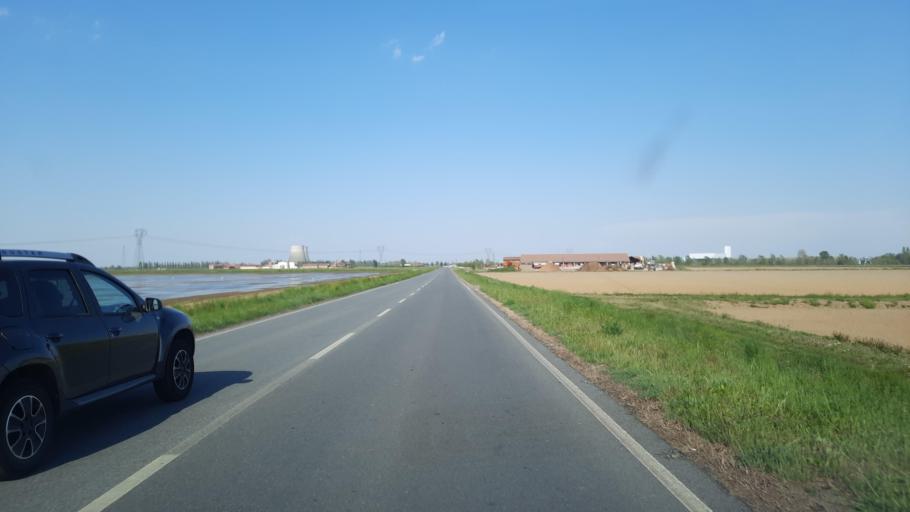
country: IT
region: Piedmont
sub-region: Provincia di Vercelli
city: Fontanetto Po
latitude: 45.2334
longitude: 8.1639
